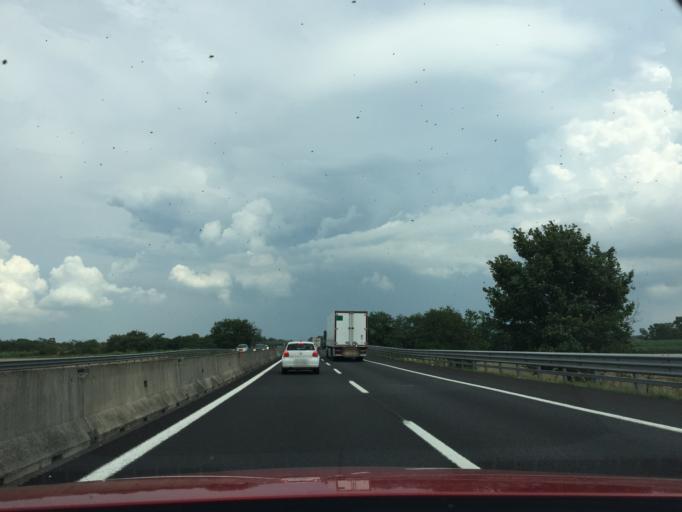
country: IT
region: Tuscany
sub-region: Provincia di Lucca
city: Porcari
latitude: 43.8179
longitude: 10.6375
